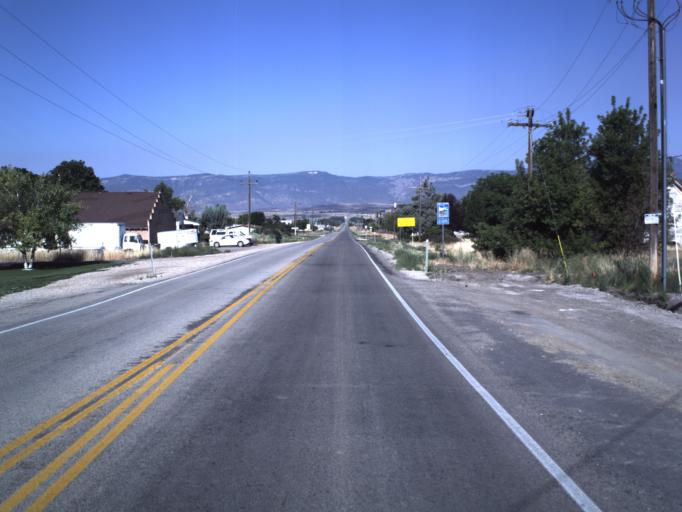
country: US
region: Utah
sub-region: Sanpete County
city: Mount Pleasant
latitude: 39.5468
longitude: -111.4654
